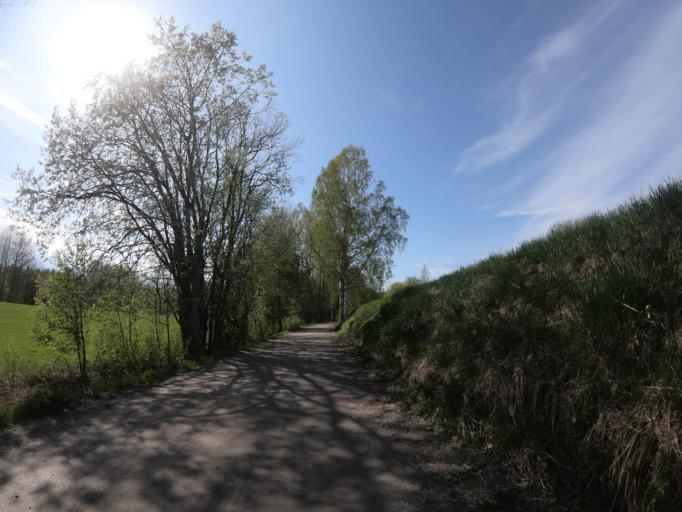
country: SE
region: Vaesterbotten
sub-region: Umea Kommun
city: Roback
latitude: 63.8293
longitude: 20.1827
